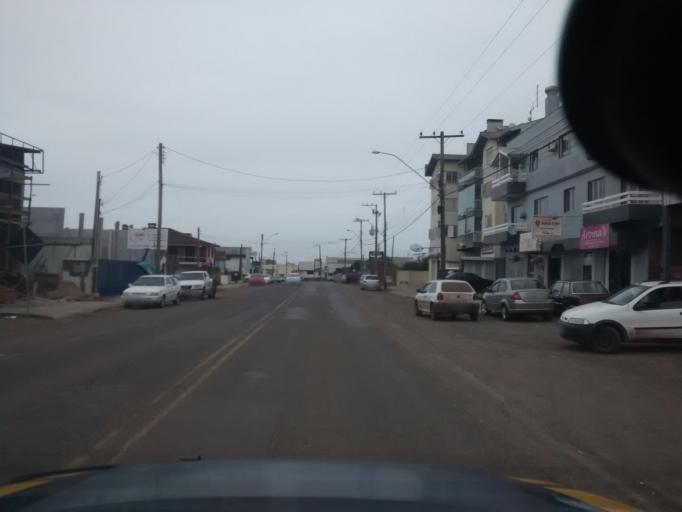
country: BR
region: Rio Grande do Sul
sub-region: Vacaria
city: Vacaria
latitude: -28.5016
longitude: -50.9499
